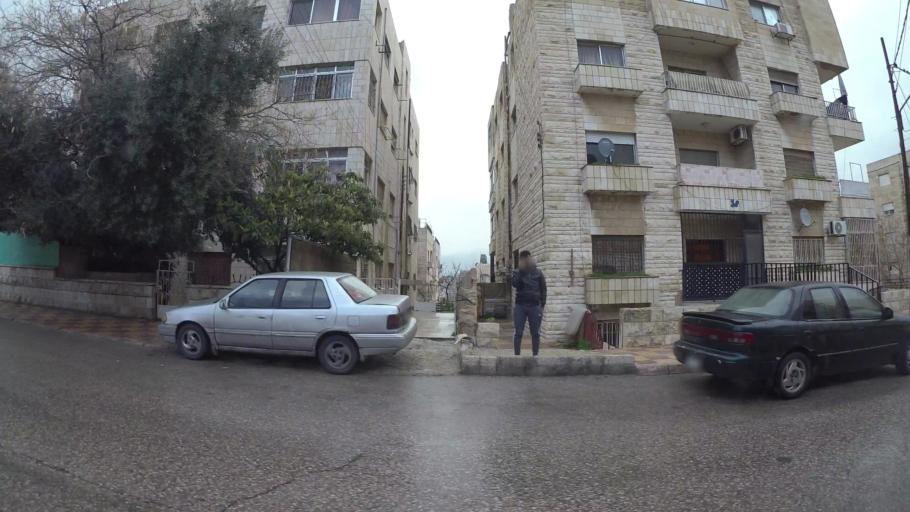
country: JO
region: Amman
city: Amman
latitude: 31.9677
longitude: 35.9222
